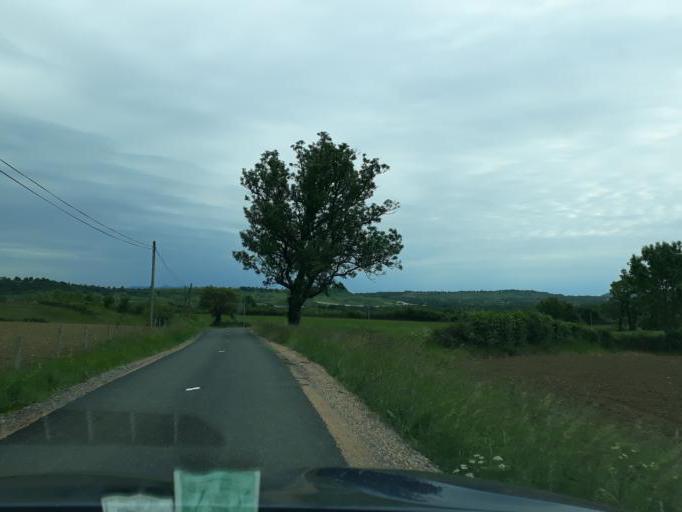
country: FR
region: Languedoc-Roussillon
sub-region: Departement de l'Herault
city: Lodeve
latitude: 43.8303
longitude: 3.2712
